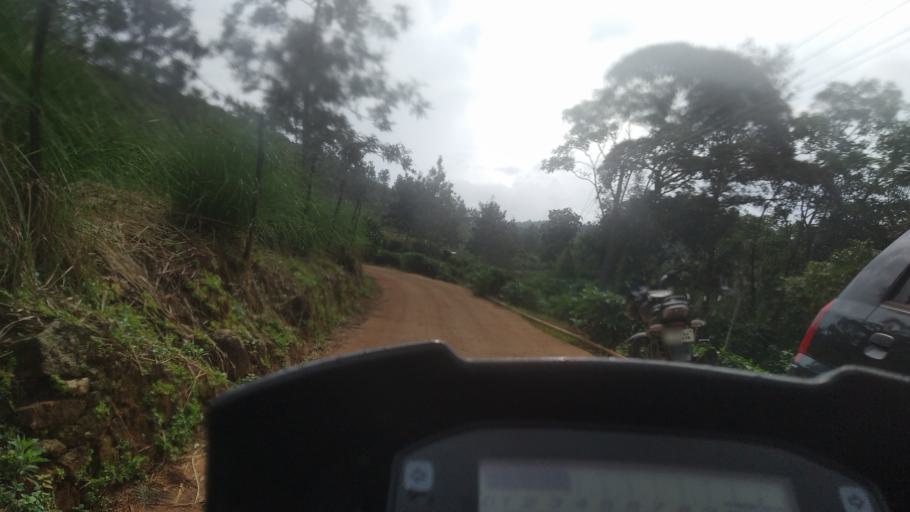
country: IN
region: Tamil Nadu
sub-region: Theni
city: Gudalur
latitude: 9.5682
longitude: 77.0889
